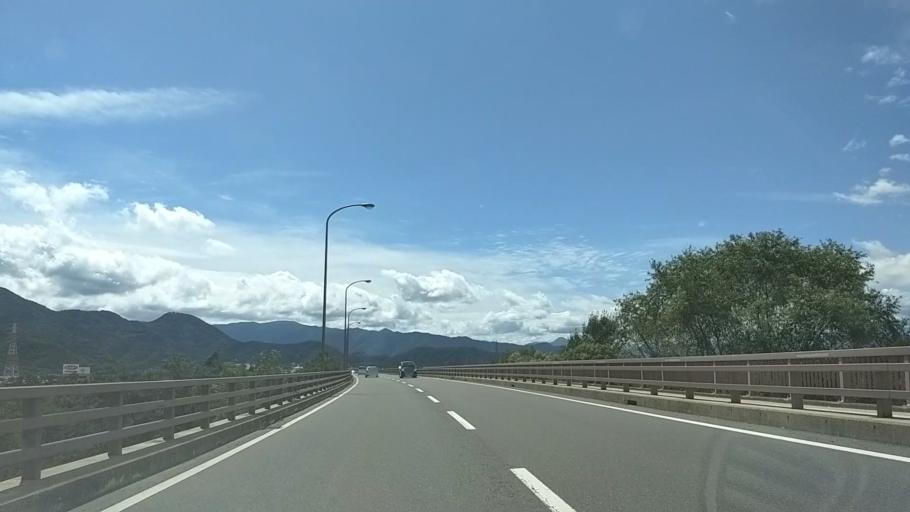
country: JP
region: Nagano
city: Nagano-shi
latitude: 36.6218
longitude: 138.2251
